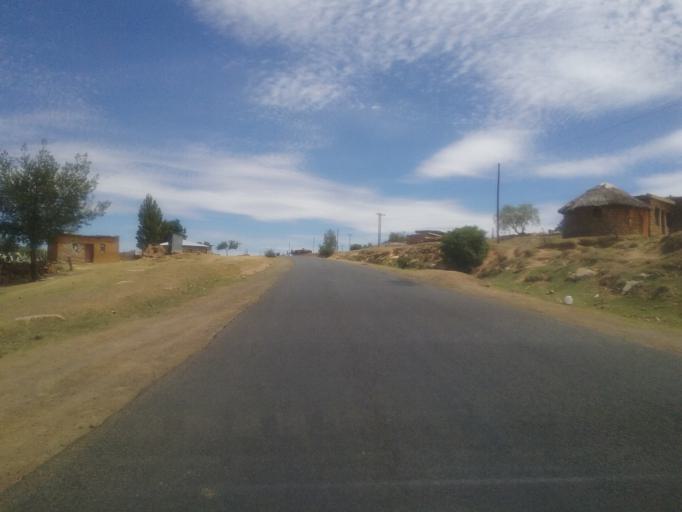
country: LS
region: Mafeteng
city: Mafeteng
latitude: -29.9923
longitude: 27.3353
